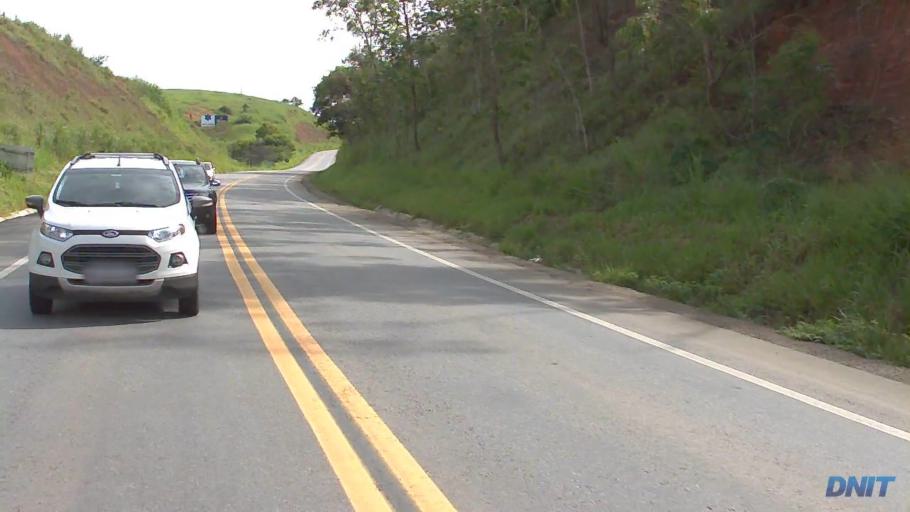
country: BR
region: Minas Gerais
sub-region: Belo Oriente
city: Belo Oriente
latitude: -19.2645
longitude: -42.3467
